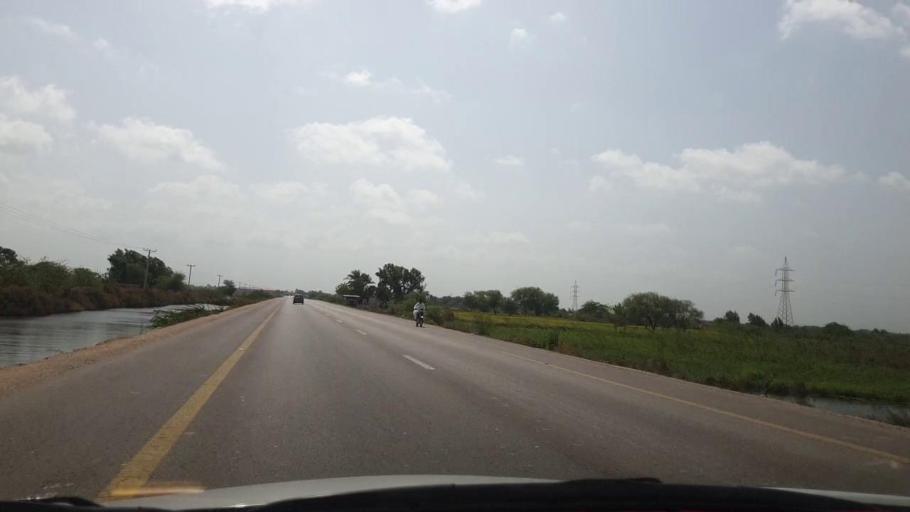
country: PK
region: Sindh
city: Talhar
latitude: 24.9210
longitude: 68.7228
